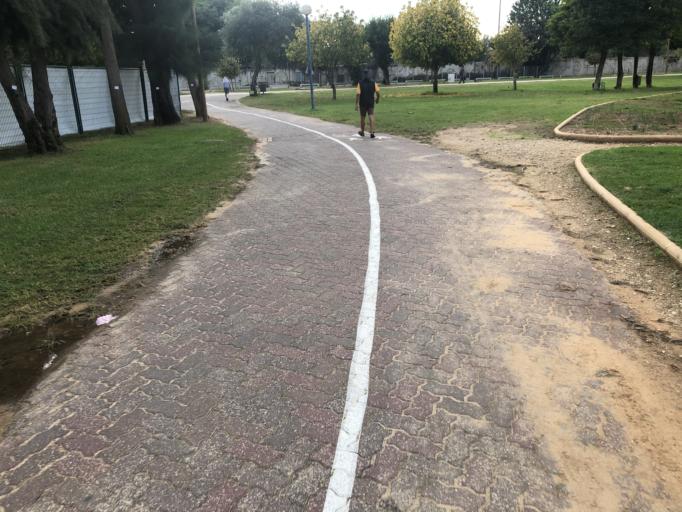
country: IL
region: Tel Aviv
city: Giv`atayim
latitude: 32.0467
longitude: 34.8236
